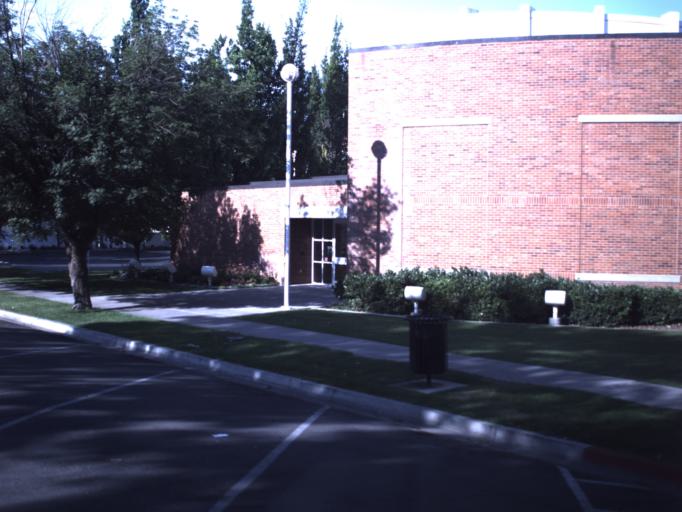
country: US
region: Utah
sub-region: Utah County
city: American Fork
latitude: 40.3758
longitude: -111.7960
